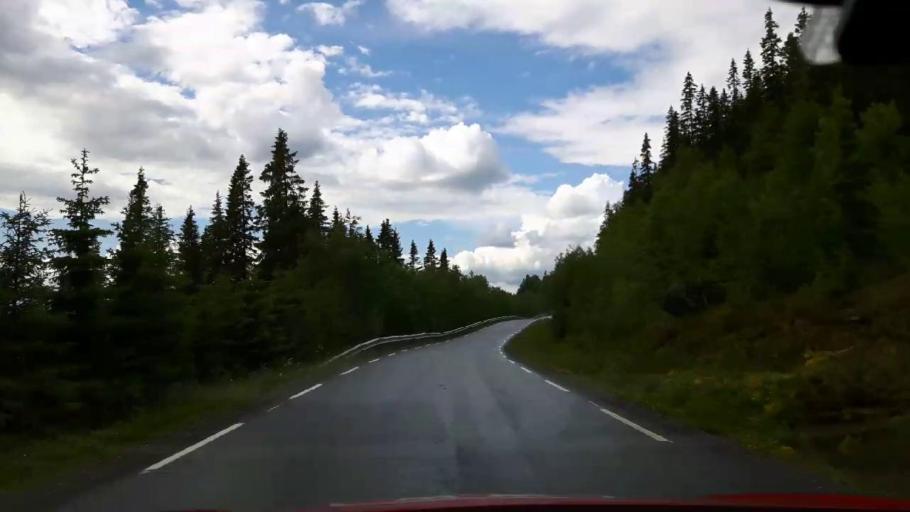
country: NO
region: Nord-Trondelag
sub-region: Lierne
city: Sandvika
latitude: 64.1038
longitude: 13.9967
